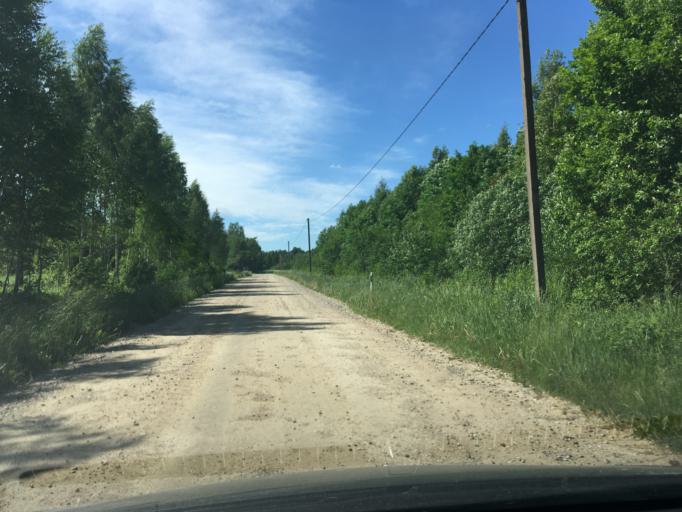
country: EE
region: Paernumaa
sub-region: Audru vald
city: Audru
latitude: 58.4560
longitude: 24.3827
